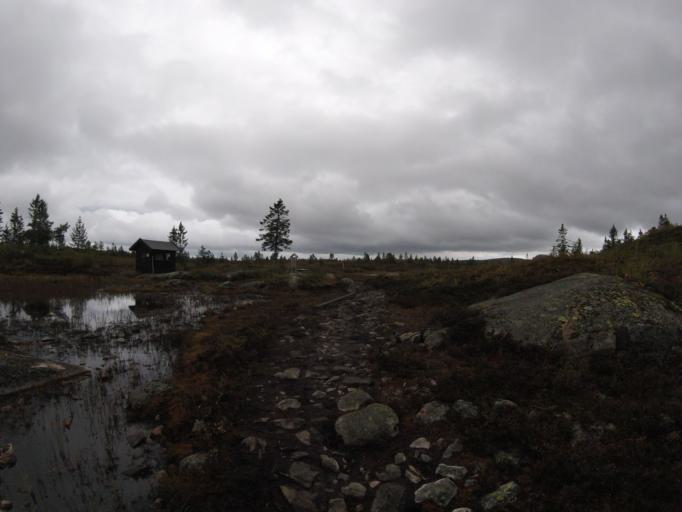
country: NO
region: Buskerud
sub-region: Flesberg
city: Lampeland
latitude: 59.7746
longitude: 9.4039
